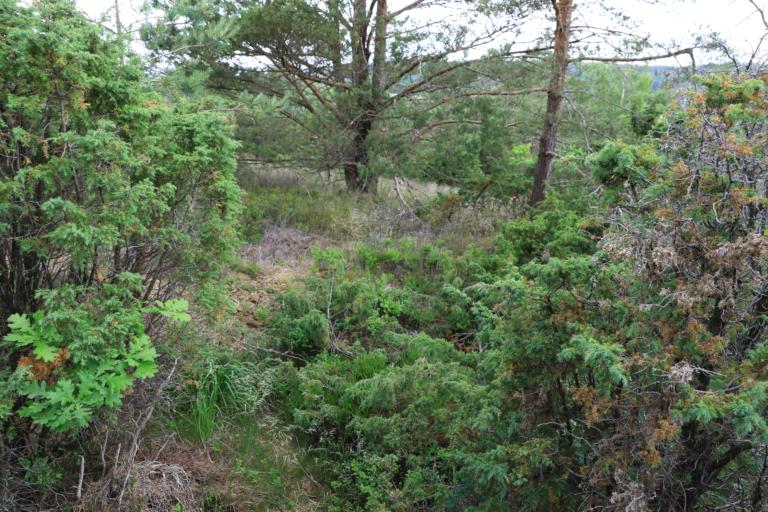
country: SE
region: Halland
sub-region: Varbergs Kommun
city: Varberg
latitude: 57.1727
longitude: 12.2558
